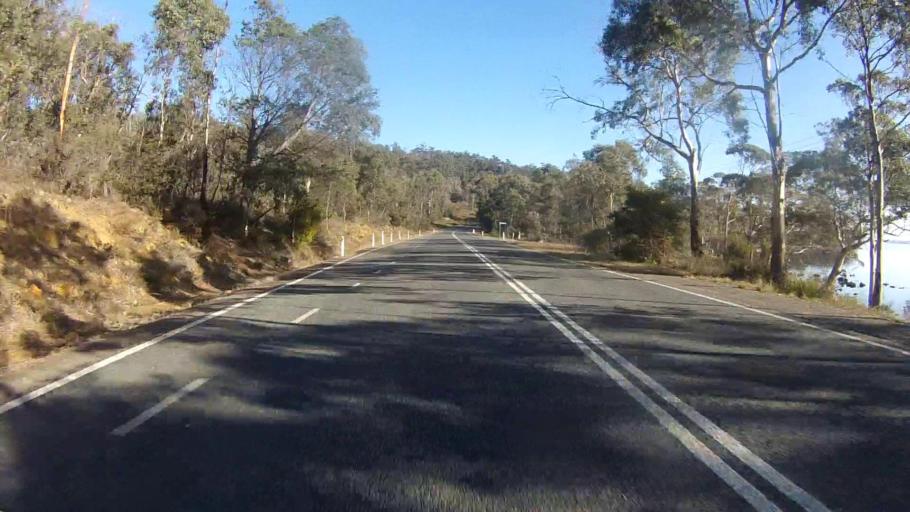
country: AU
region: Tasmania
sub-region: Clarence
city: Sandford
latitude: -43.0243
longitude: 147.8842
